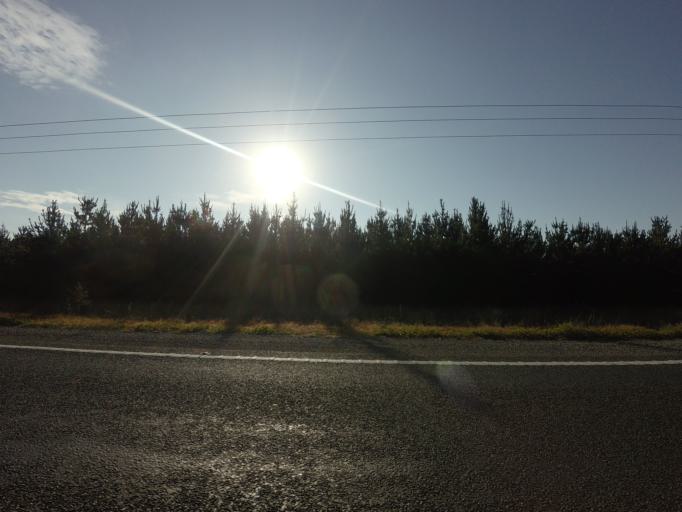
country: AU
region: Tasmania
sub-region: Northern Midlands
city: Longford
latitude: -41.5446
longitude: 147.0568
